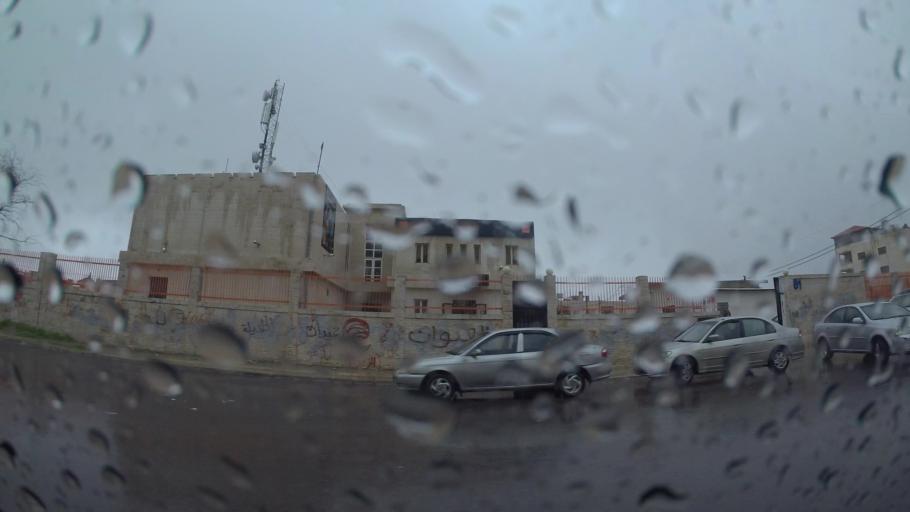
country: JO
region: Amman
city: Al Jubayhah
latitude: 32.0485
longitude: 35.8879
